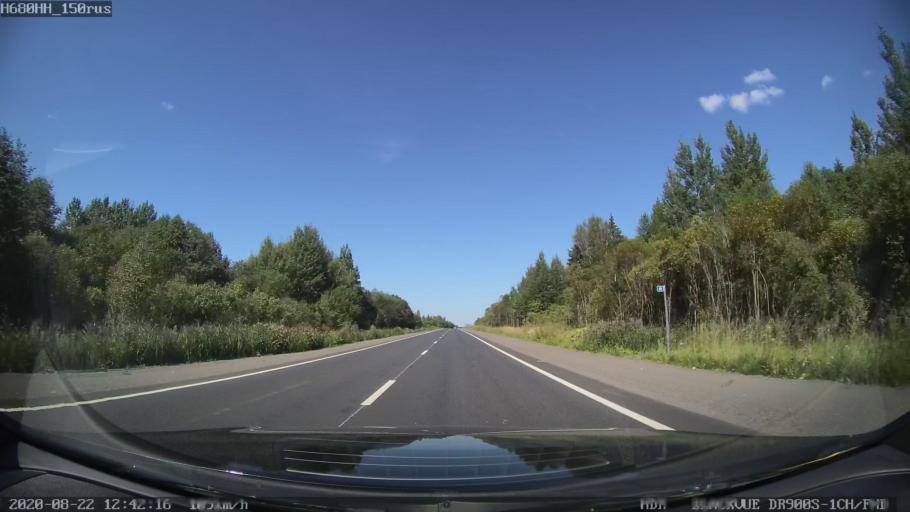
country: RU
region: Tverskaya
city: Rameshki
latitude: 57.3594
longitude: 36.0947
